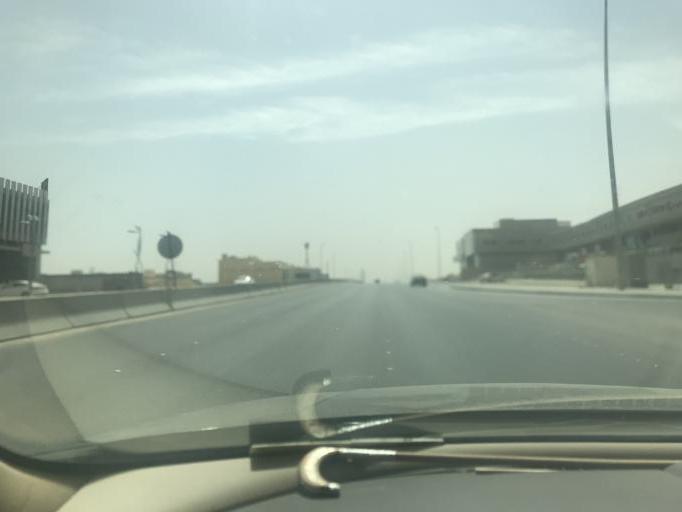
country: SA
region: Ar Riyad
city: Riyadh
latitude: 24.8180
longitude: 46.6878
